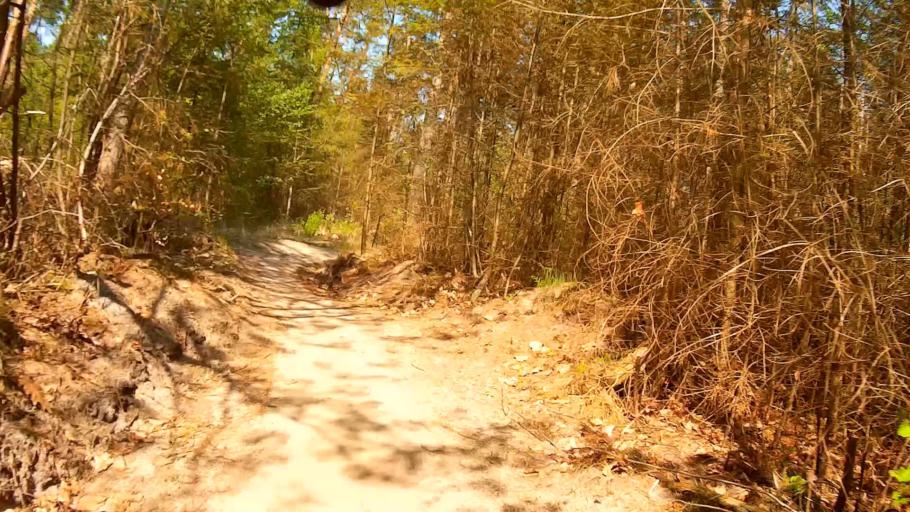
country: NL
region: Utrecht
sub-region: Gemeente Baarn
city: Baarn
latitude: 52.1929
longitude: 5.2552
